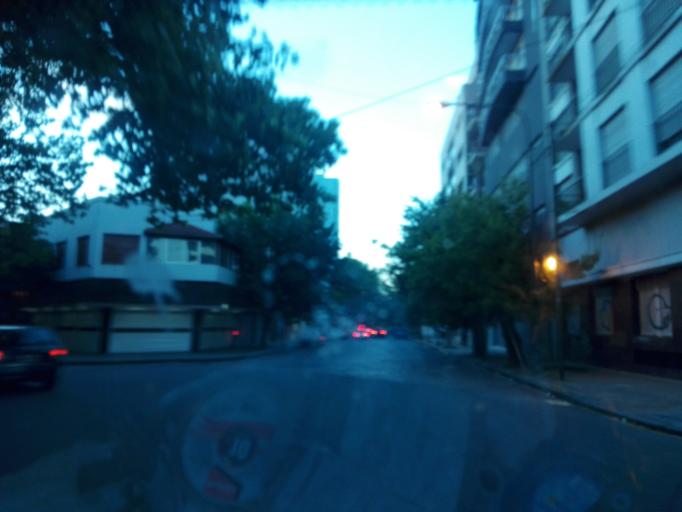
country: AR
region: Buenos Aires
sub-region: Partido de La Plata
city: La Plata
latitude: -34.9101
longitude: -57.9492
